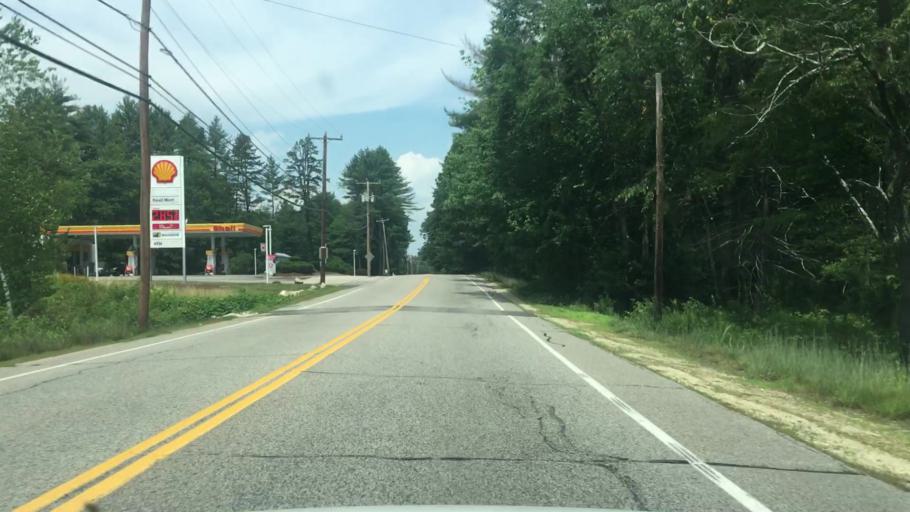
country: US
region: New Hampshire
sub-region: Strafford County
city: Rochester
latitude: 43.3584
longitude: -70.9803
